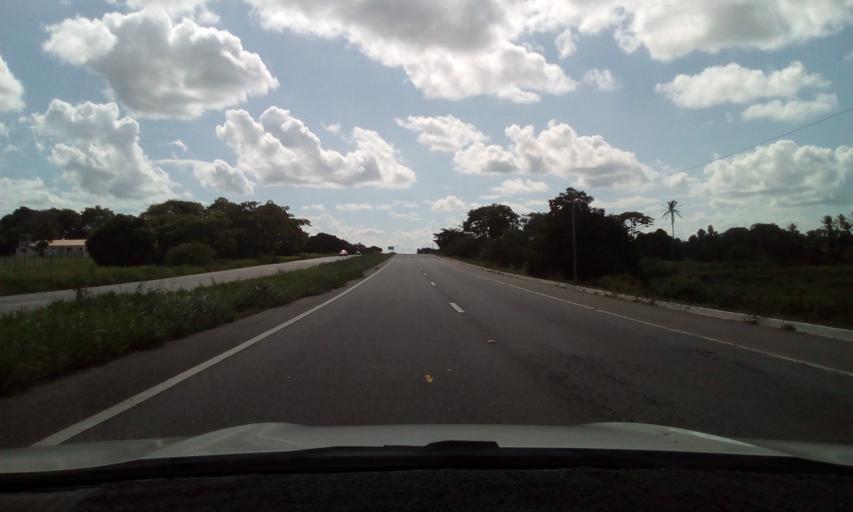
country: BR
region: Paraiba
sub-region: Pilar
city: Pilar
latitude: -7.1900
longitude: -35.2515
